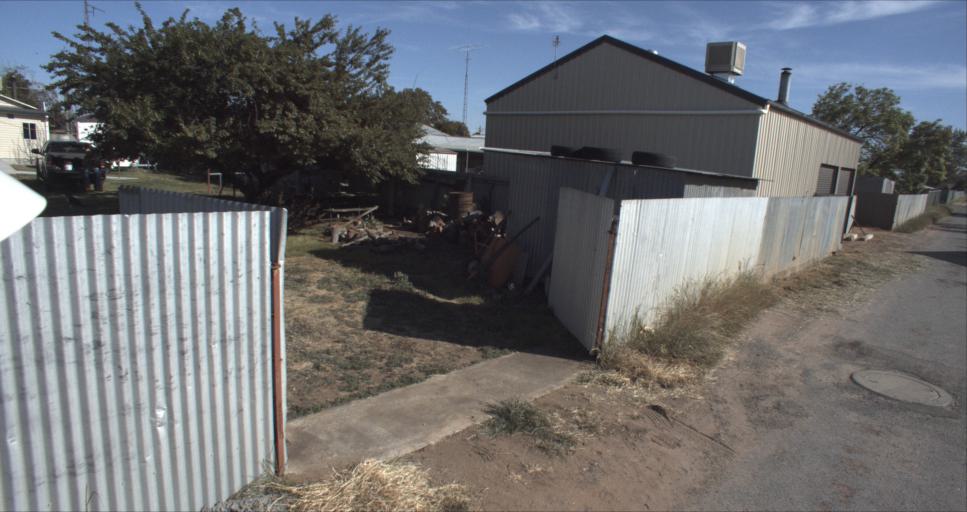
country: AU
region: New South Wales
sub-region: Leeton
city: Leeton
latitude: -34.6014
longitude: 146.4098
